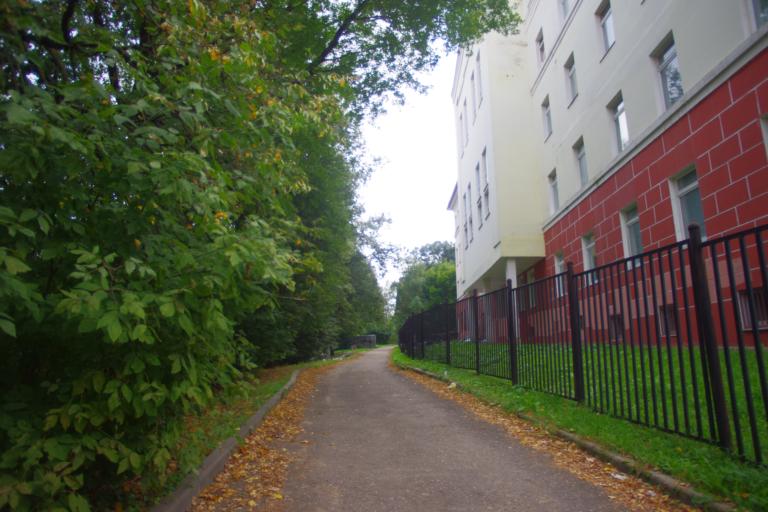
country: RU
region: Moskovskaya
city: Krasnogorsk
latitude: 55.8349
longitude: 37.3254
